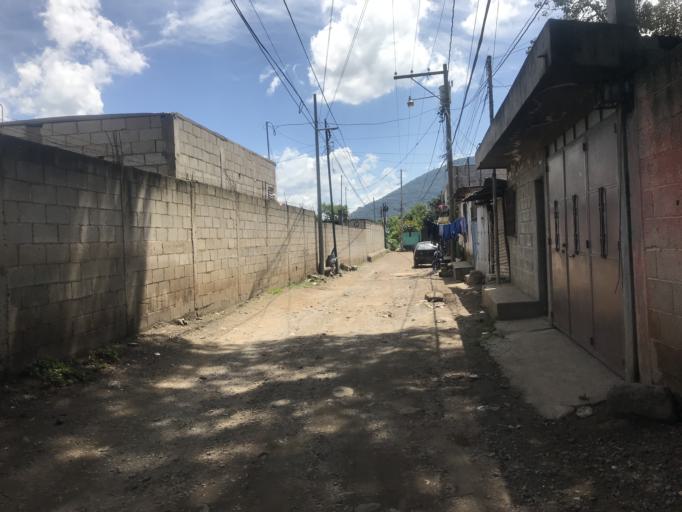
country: GT
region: Guatemala
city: Amatitlan
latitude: 14.4803
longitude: -90.6337
